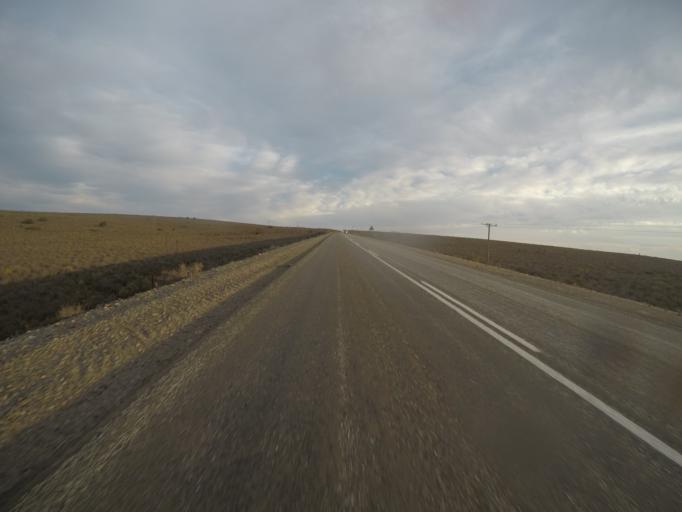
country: ZA
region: Eastern Cape
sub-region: Cacadu District Municipality
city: Willowmore
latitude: -33.5780
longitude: 23.1673
